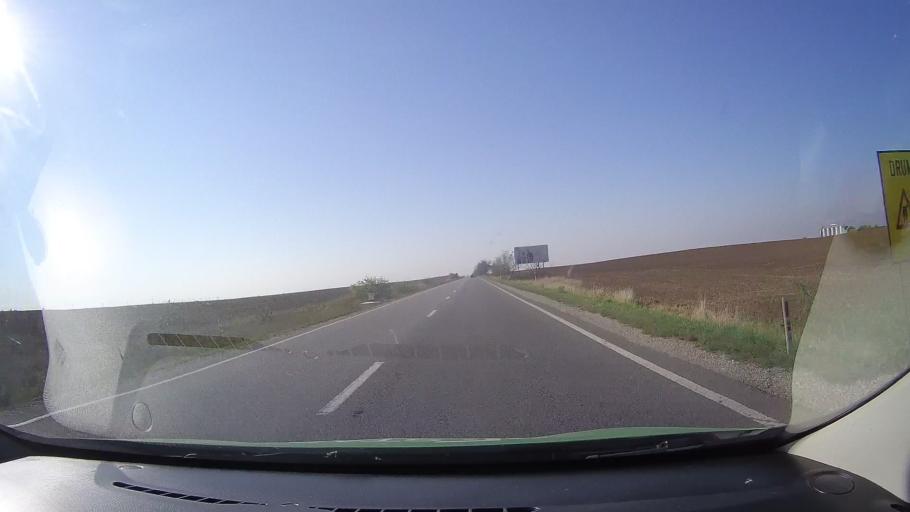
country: RO
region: Satu Mare
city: Carei
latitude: 47.6643
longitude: 22.4332
